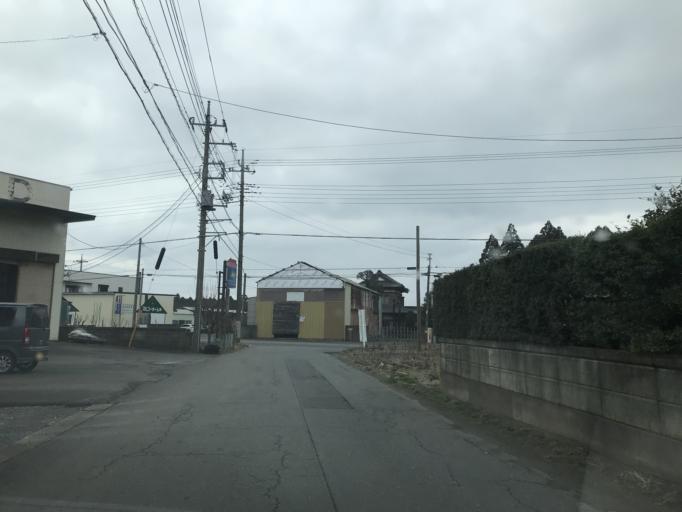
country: JP
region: Chiba
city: Sawara
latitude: 35.8603
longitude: 140.5506
